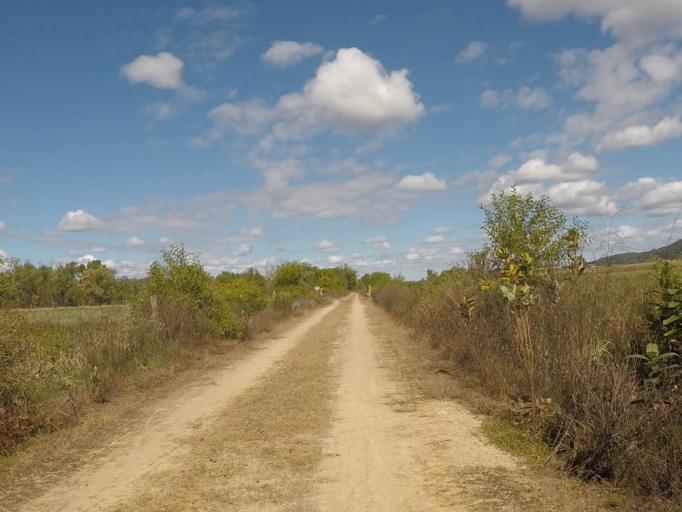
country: US
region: Wisconsin
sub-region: Richland County
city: Richland Center
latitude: 43.2347
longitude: -90.3002
